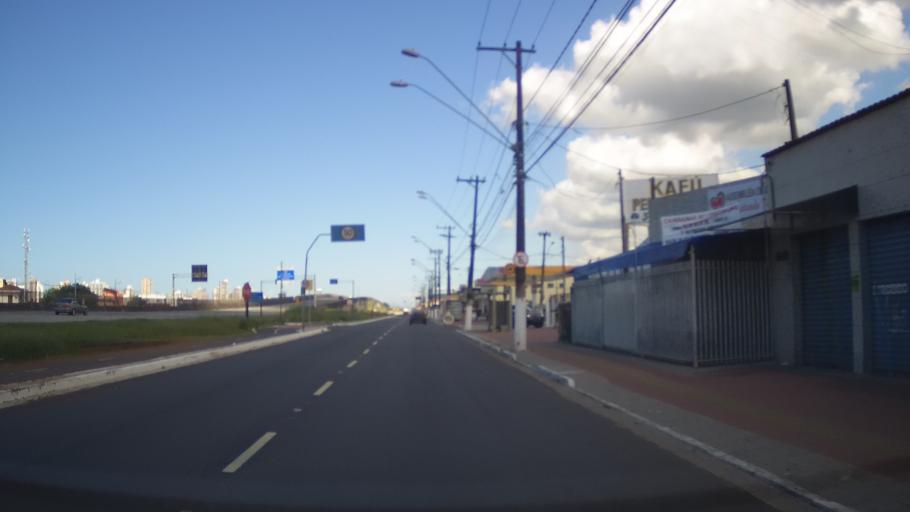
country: BR
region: Sao Paulo
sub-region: Praia Grande
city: Praia Grande
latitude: -24.0363
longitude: -46.5159
